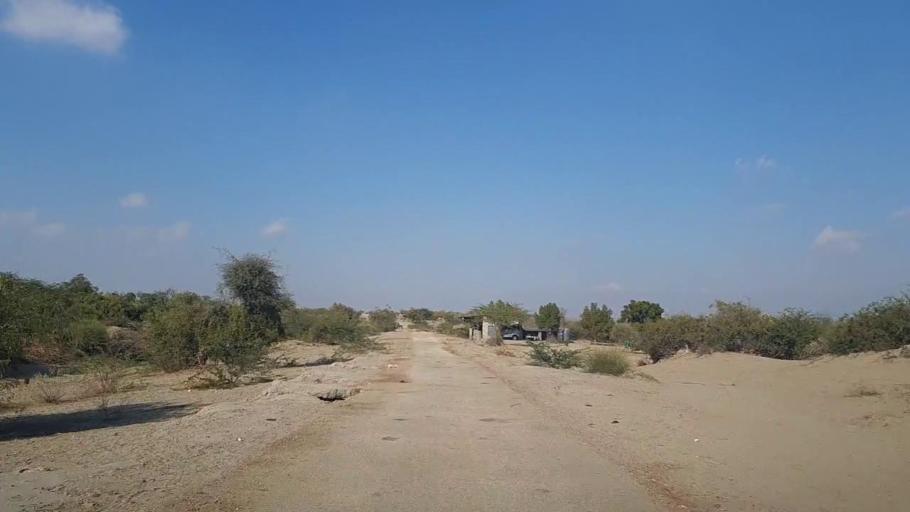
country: PK
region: Sindh
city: Tando Mittha Khan
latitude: 26.0191
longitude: 69.2505
